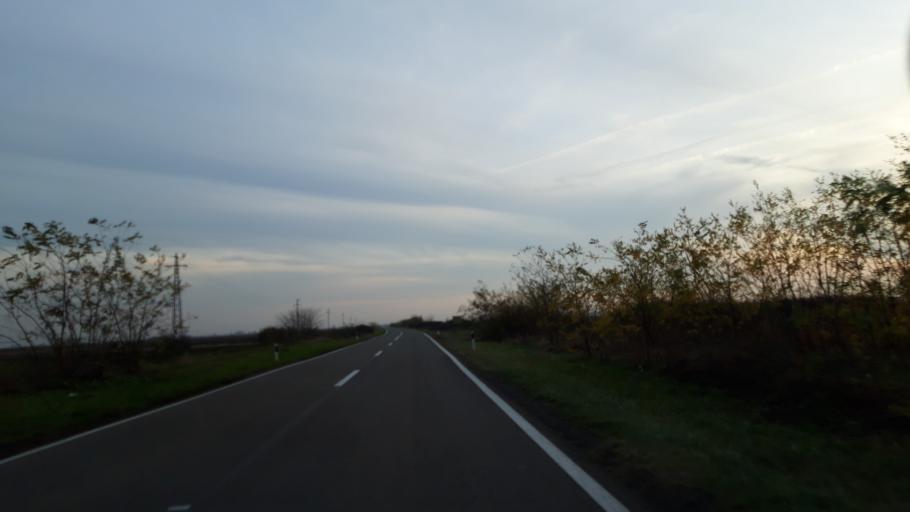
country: RS
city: Ostojicevo
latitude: 45.8634
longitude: 20.1647
